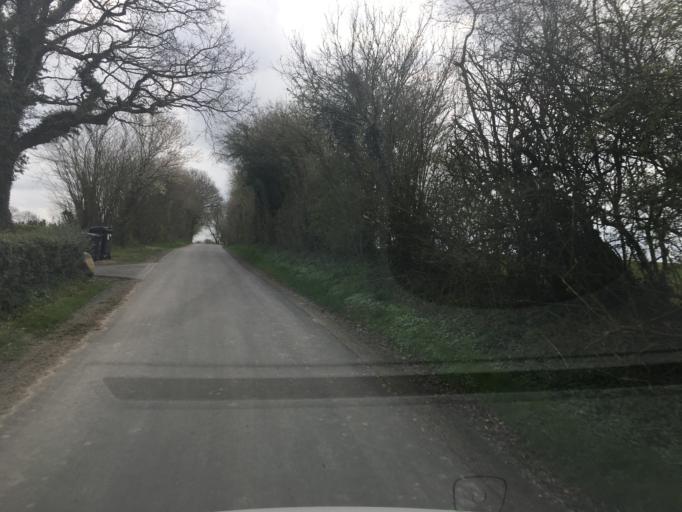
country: DE
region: Schleswig-Holstein
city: Glucksburg
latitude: 54.9004
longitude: 9.5273
